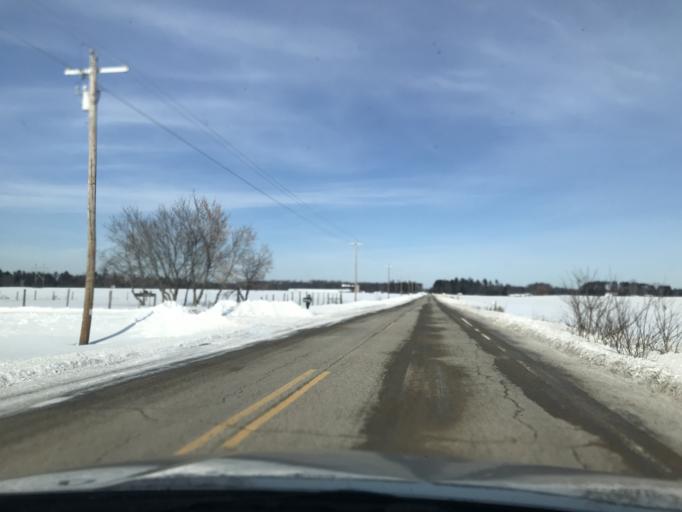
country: US
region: Wisconsin
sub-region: Oconto County
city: Oconto Falls
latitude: 45.1264
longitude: -88.1778
